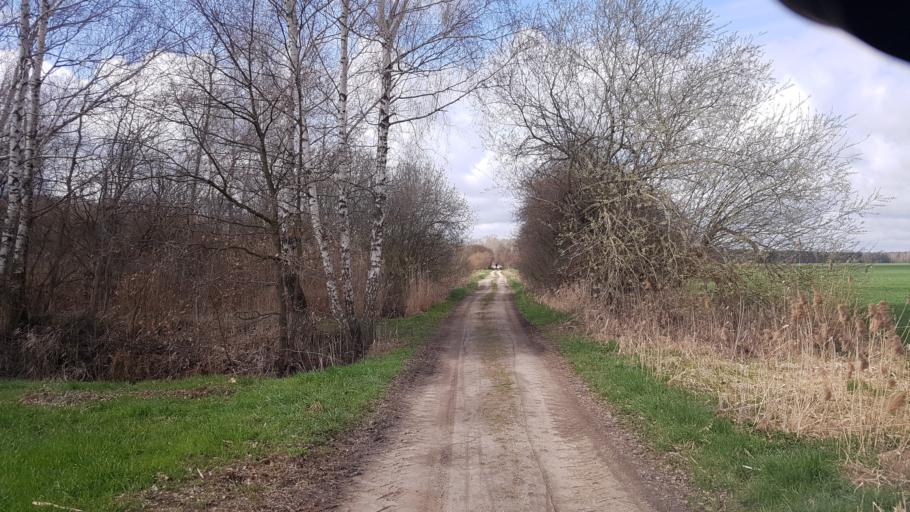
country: DE
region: Brandenburg
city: Doberlug-Kirchhain
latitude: 51.6474
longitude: 13.5331
